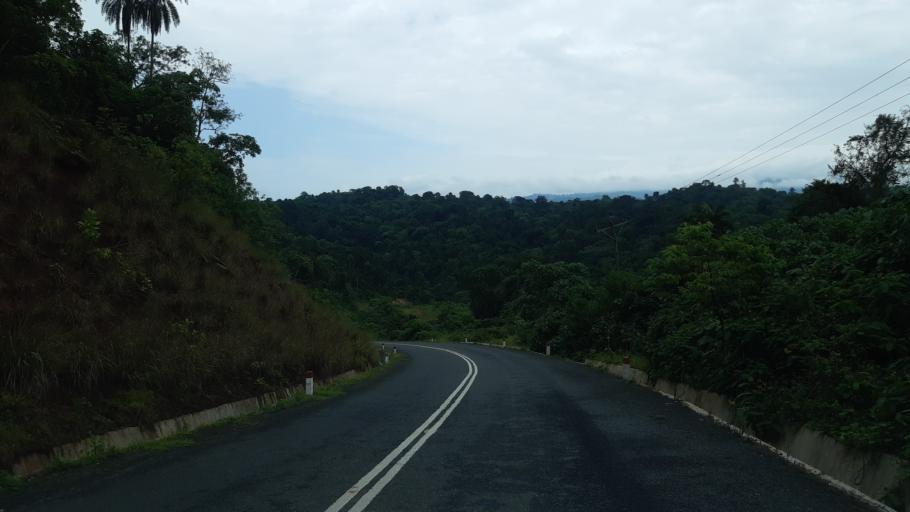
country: ET
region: Southern Nations, Nationalities, and People's Region
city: Bonga
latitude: 7.2022
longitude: 36.2787
